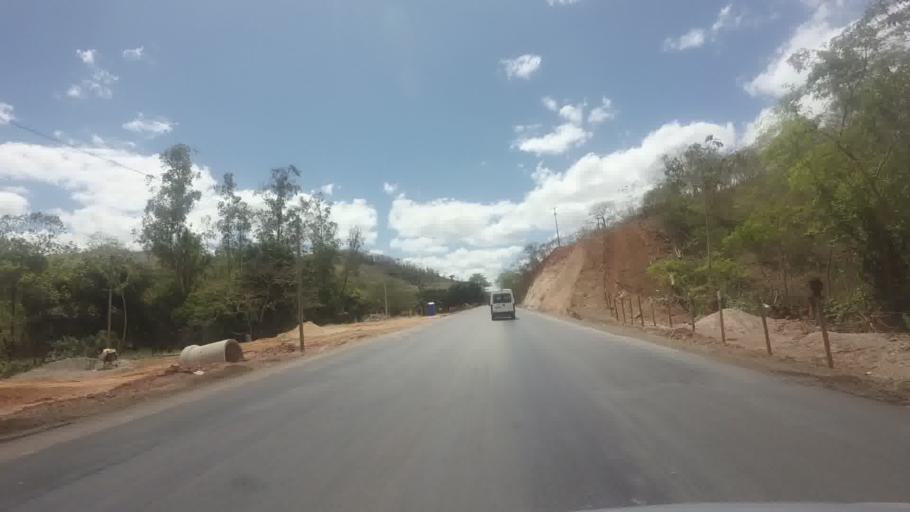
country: BR
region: Rio de Janeiro
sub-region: Santo Antonio De Padua
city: Santo Antonio de Padua
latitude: -21.5052
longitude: -42.0823
